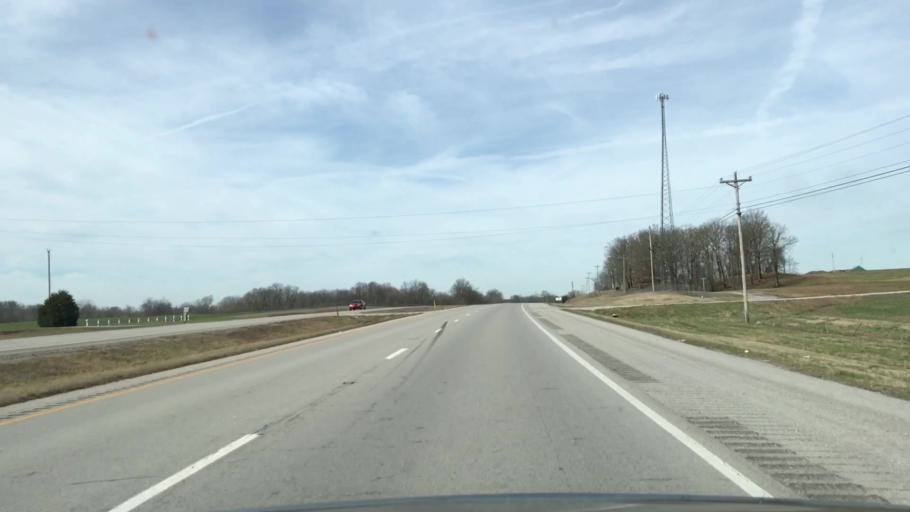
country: US
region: Kentucky
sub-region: Christian County
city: Hopkinsville
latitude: 36.8802
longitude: -87.5912
